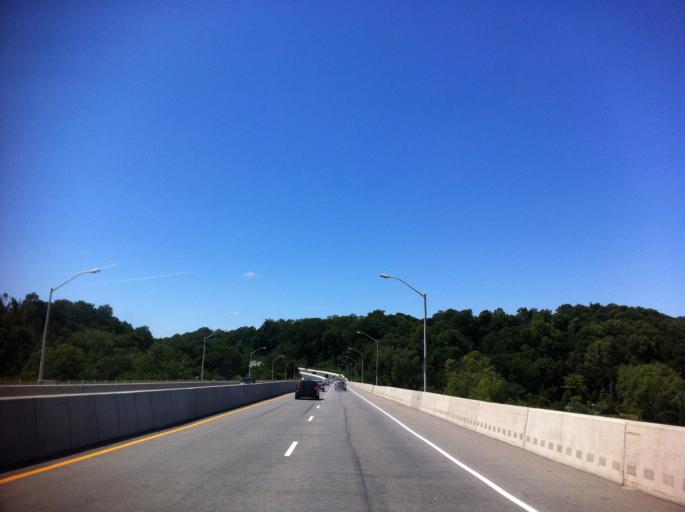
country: US
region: New York
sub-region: Nassau County
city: Roslyn
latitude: 40.8039
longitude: -73.6500
